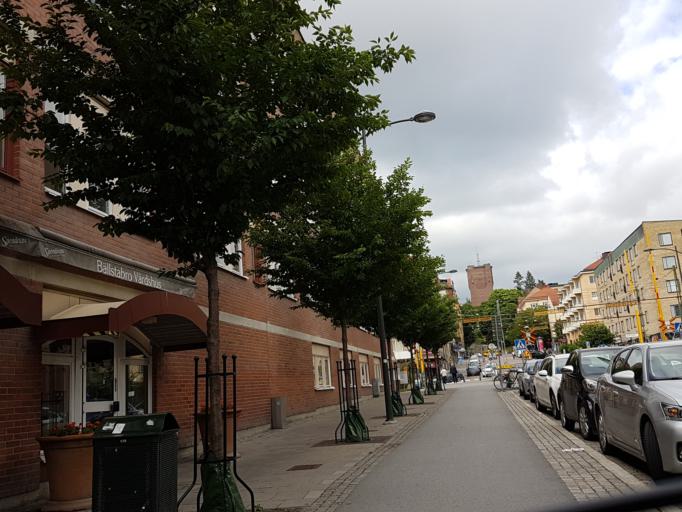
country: SE
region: Stockholm
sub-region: Sundbybergs Kommun
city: Sundbyberg
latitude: 59.3623
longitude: 17.9651
